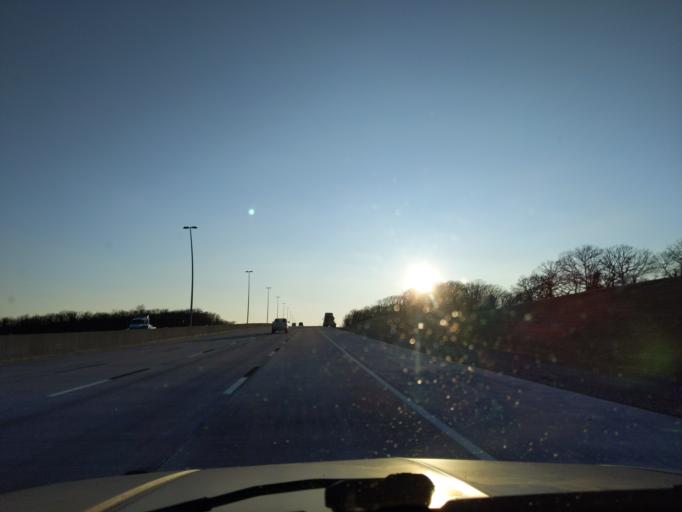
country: US
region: Oklahoma
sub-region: Creek County
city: Kellyville
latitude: 35.9348
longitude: -96.2667
